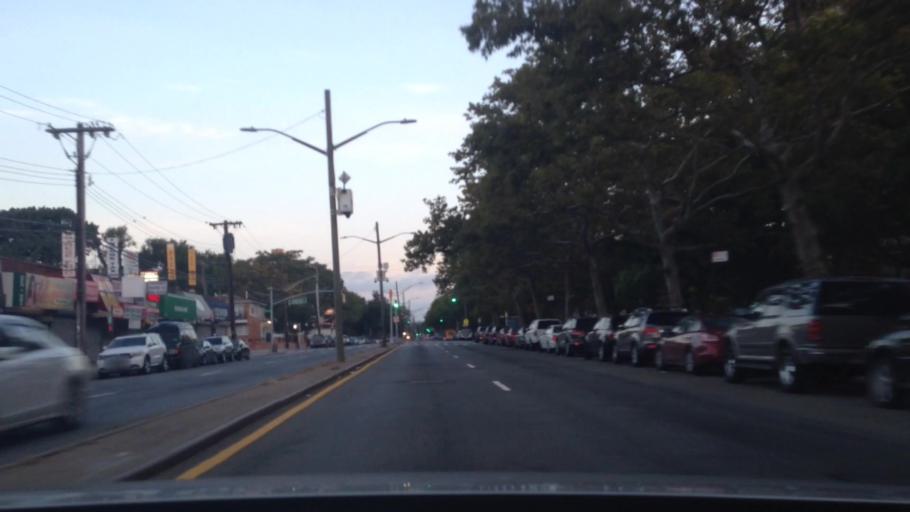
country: US
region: New York
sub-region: Queens County
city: Jamaica
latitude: 40.6726
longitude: -73.7751
